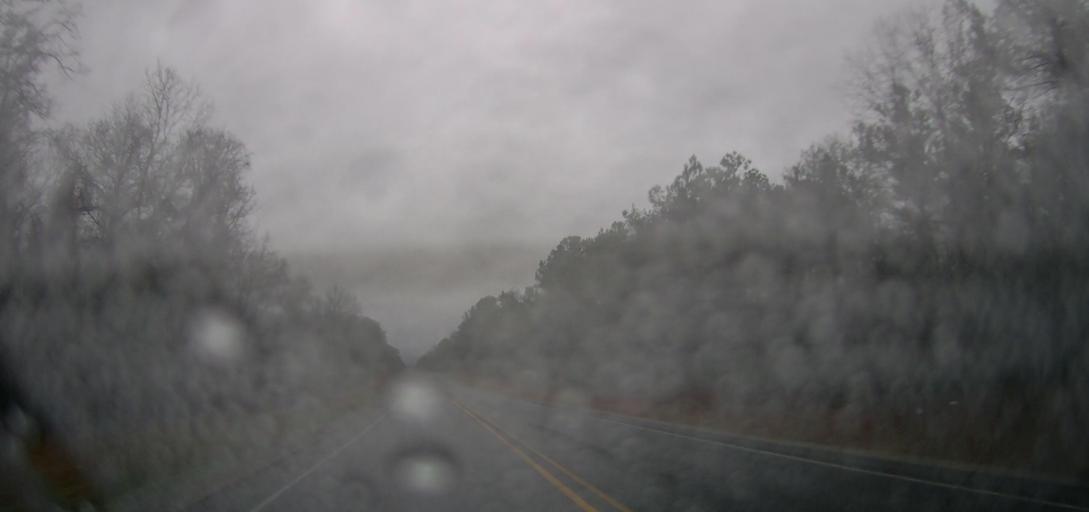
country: US
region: Alabama
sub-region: Autauga County
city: Pine Level
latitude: 32.5943
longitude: -86.7059
